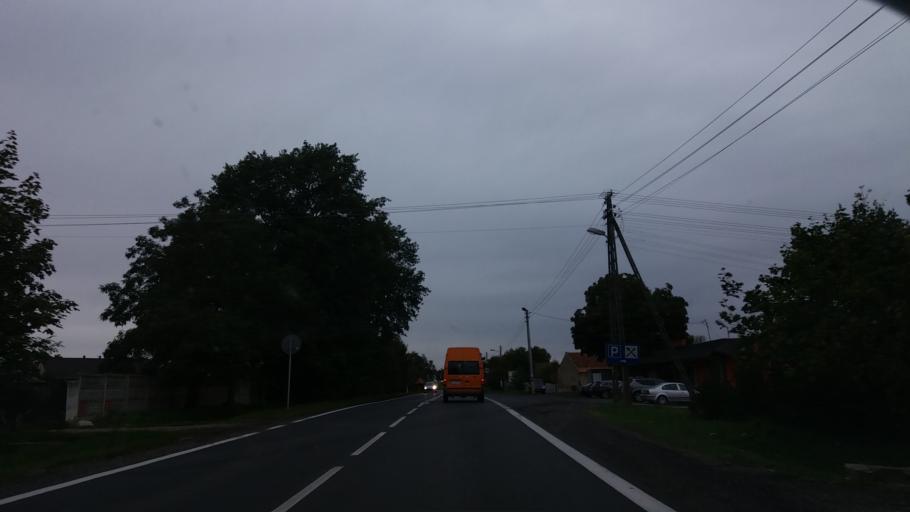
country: PL
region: Lower Silesian Voivodeship
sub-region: Powiat legnicki
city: Prochowice
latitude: 51.3148
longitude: 16.3258
